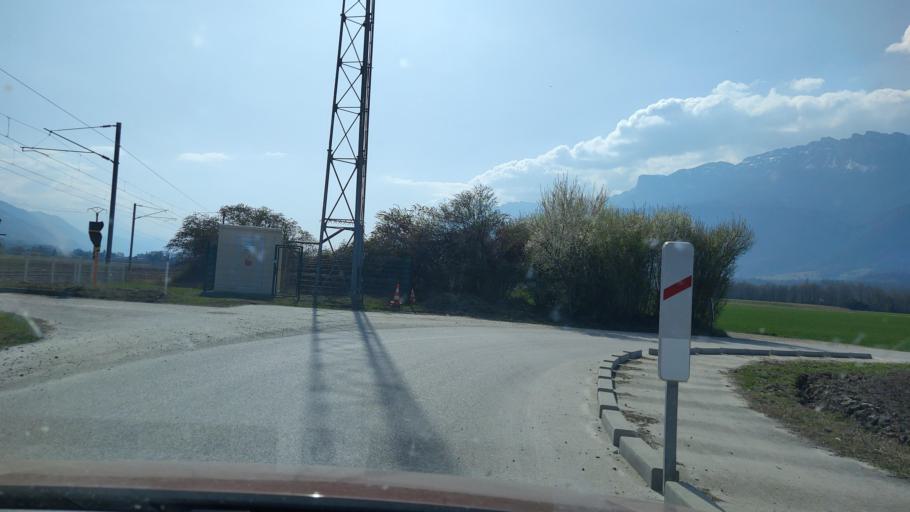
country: FR
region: Rhone-Alpes
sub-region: Departement de l'Isere
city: Pontcharra
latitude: 45.4565
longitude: 6.0244
